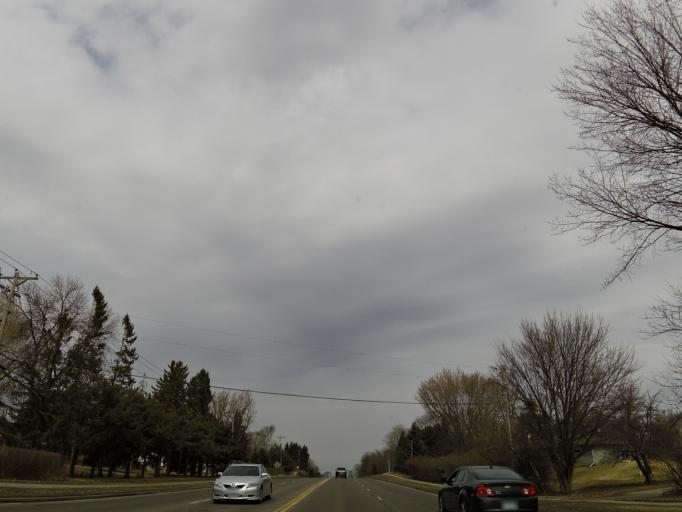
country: US
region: Minnesota
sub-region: Hennepin County
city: Bloomington
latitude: 44.8204
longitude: -93.3295
